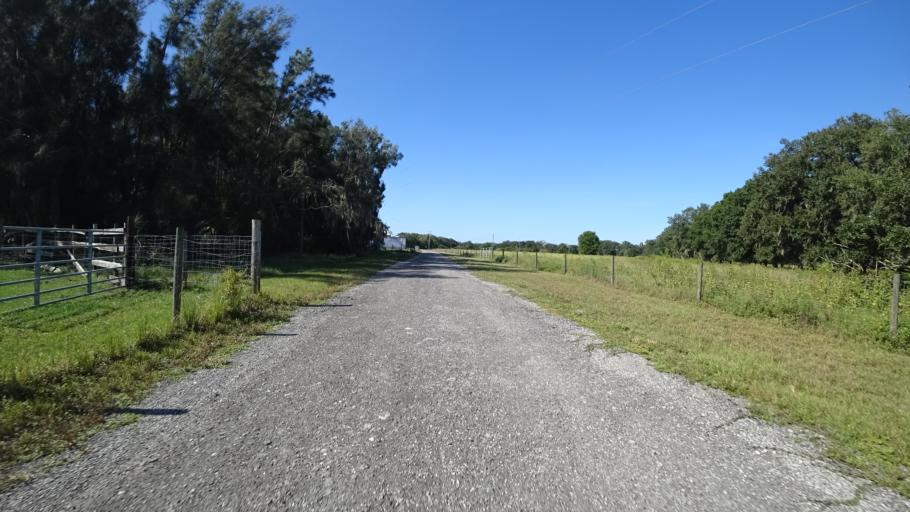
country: US
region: Florida
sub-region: Hillsborough County
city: Wimauma
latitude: 27.5985
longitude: -82.1866
